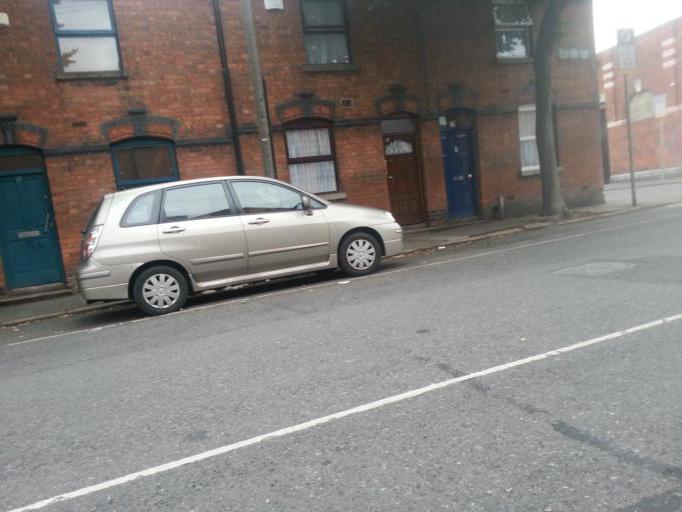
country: IE
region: Leinster
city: Rathmines
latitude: 53.3420
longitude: -6.2736
